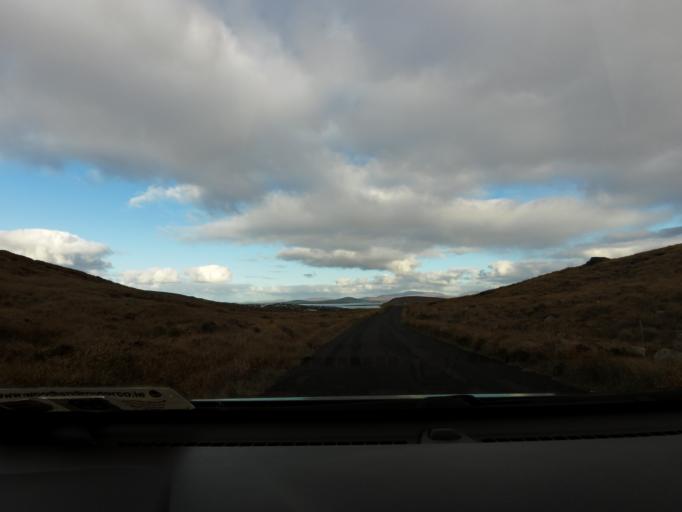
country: IE
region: Connaught
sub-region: Maigh Eo
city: Belmullet
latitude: 53.9392
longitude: -9.9897
